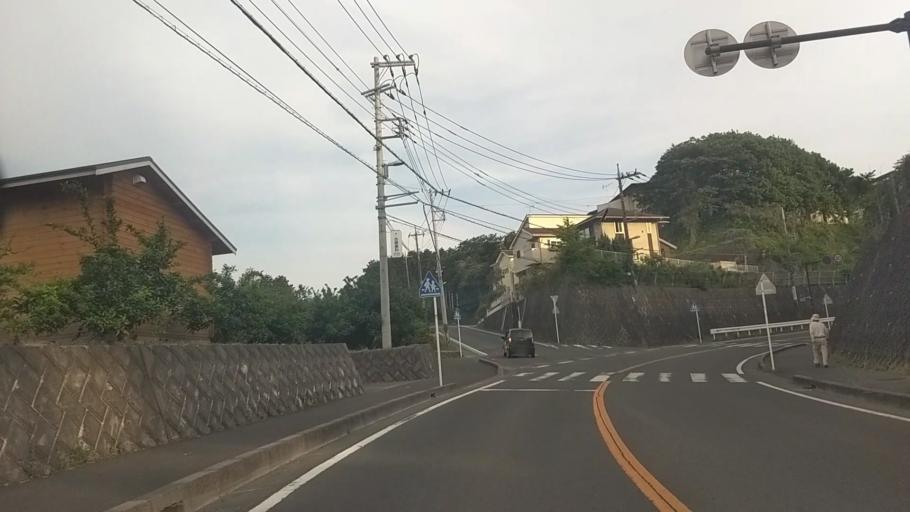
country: JP
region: Kanagawa
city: Odawara
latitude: 35.3267
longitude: 139.1071
